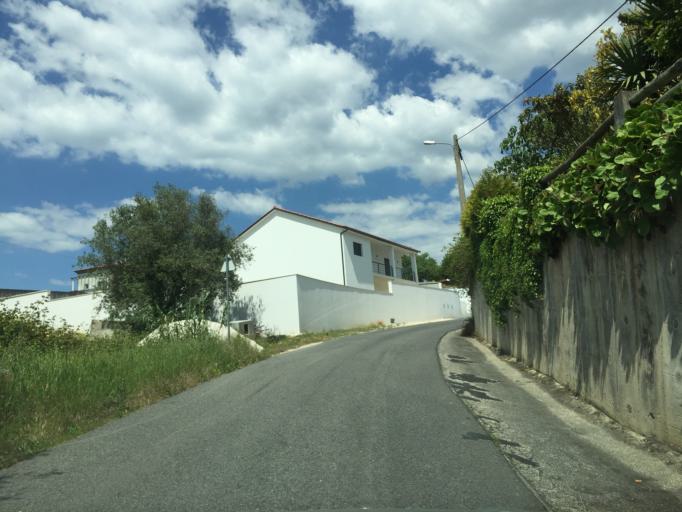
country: PT
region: Santarem
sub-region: Ourem
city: Ourem
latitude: 39.6696
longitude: -8.5752
